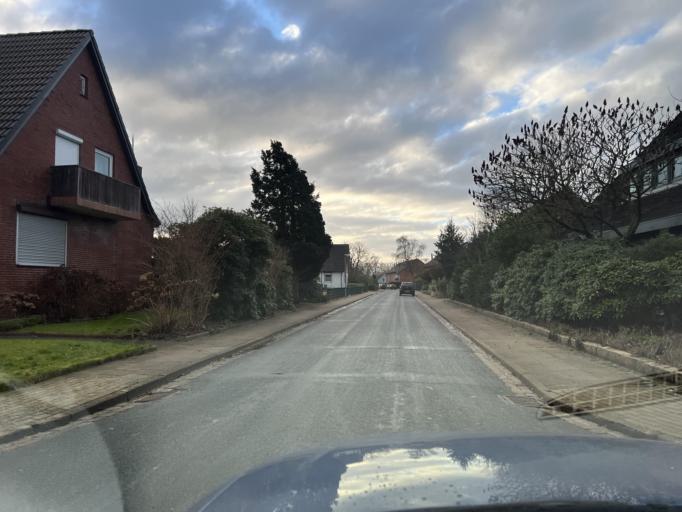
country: DE
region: Schleswig-Holstein
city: Heide
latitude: 54.2009
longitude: 9.1075
